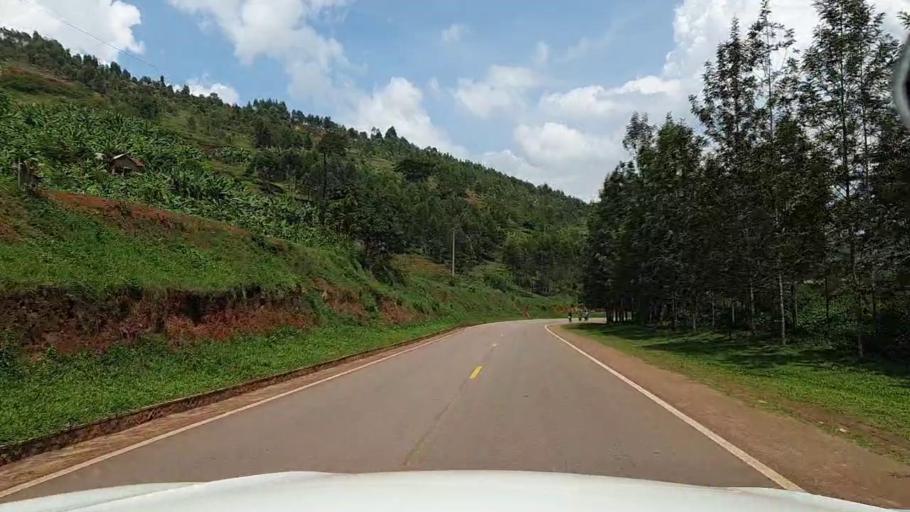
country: RW
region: Kigali
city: Kigali
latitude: -1.8327
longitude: 30.0789
